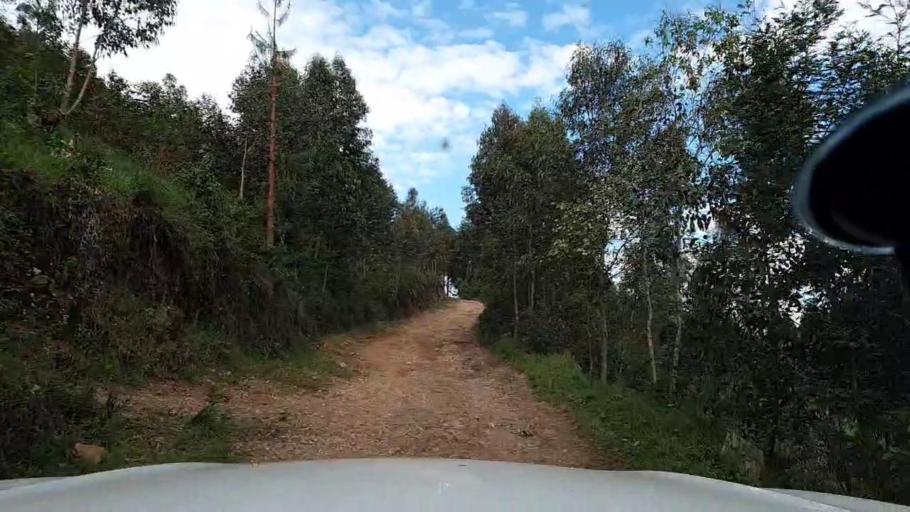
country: RW
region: Kigali
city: Kigali
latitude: -1.7851
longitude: 29.8327
